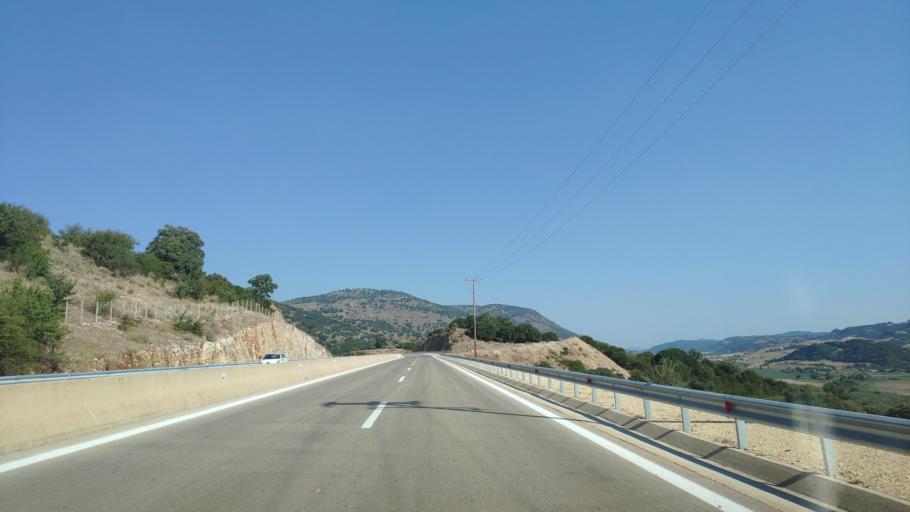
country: GR
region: West Greece
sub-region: Nomos Aitolias kai Akarnanias
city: Katouna
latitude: 38.8438
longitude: 21.1030
